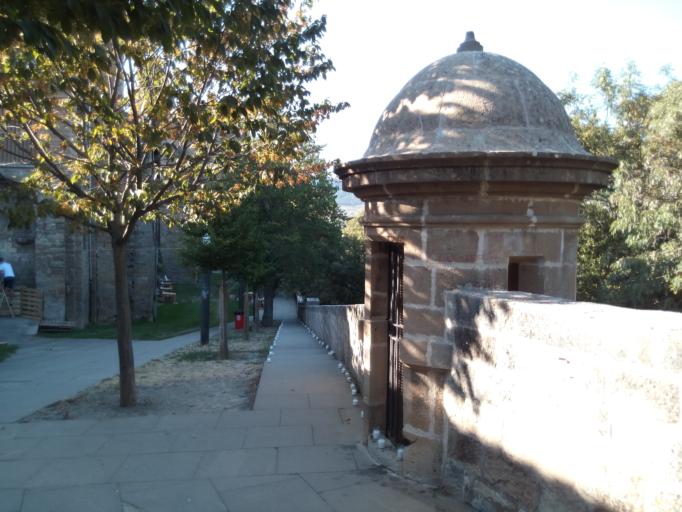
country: ES
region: Navarre
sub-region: Provincia de Navarra
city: Pamplona
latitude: 42.8188
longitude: -1.6396
